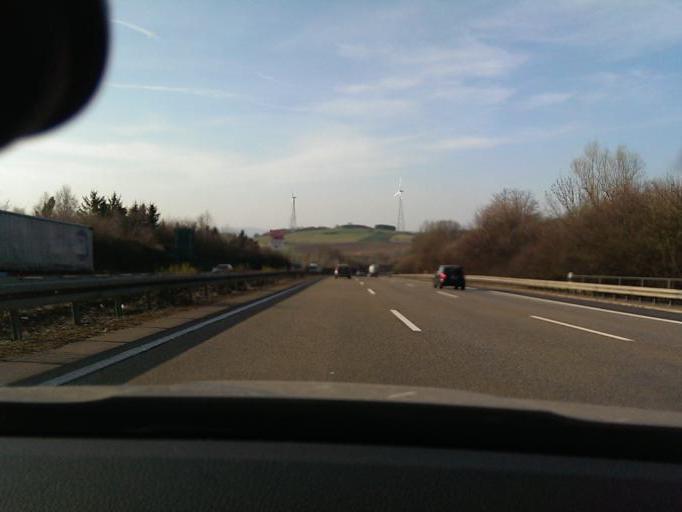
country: DE
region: Hesse
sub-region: Regierungsbezirk Kassel
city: Malsfeld
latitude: 51.0787
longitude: 9.4872
